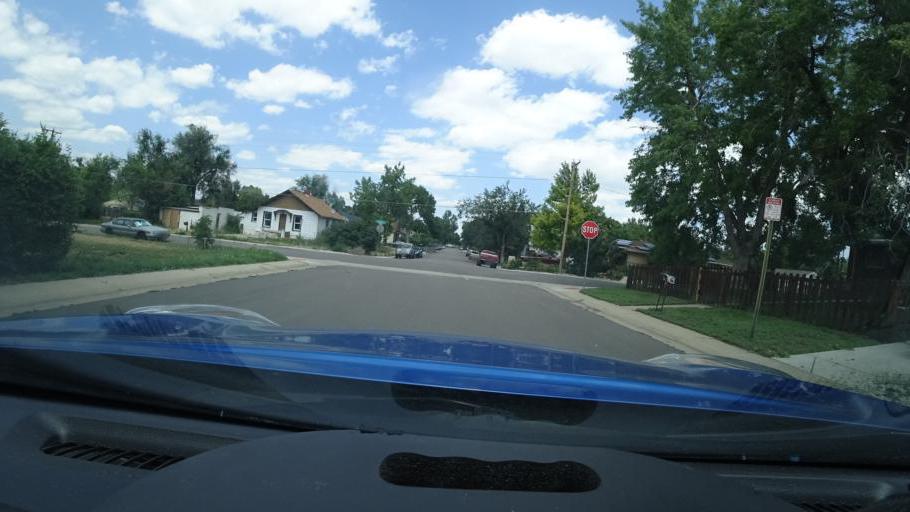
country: US
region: Colorado
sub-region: Arapahoe County
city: Englewood
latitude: 39.6800
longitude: -104.9949
